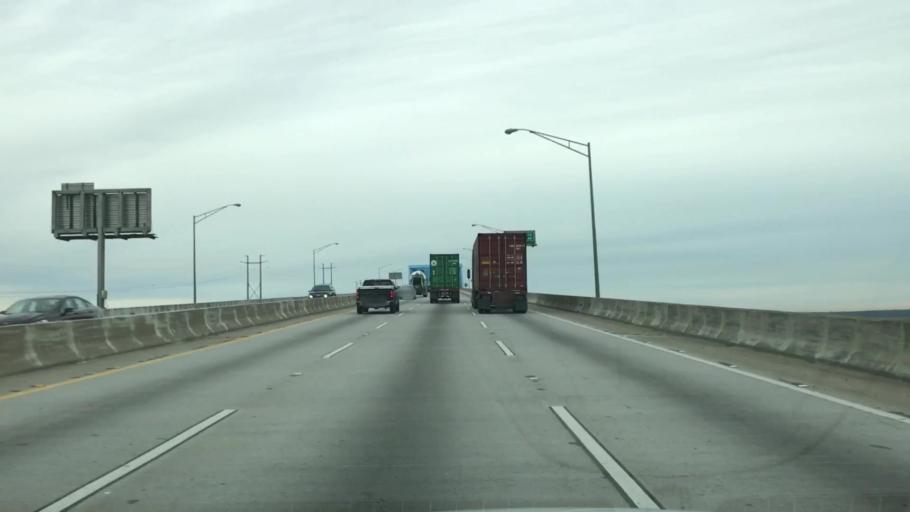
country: US
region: South Carolina
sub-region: Charleston County
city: North Charleston
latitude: 32.8923
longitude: -79.9717
